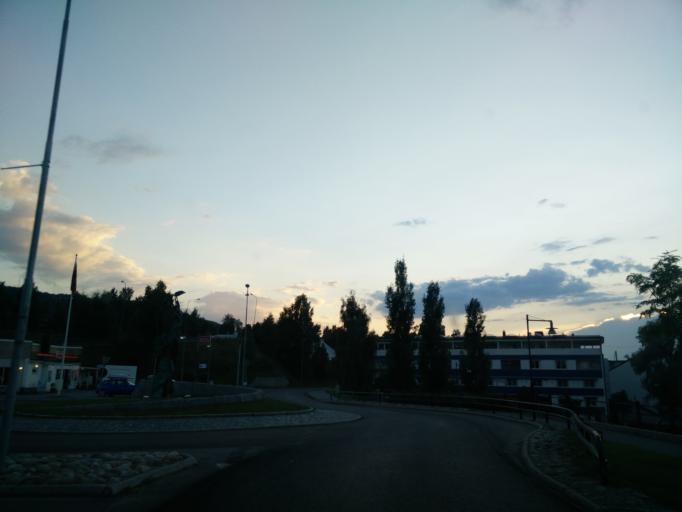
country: SE
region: Vaesternorrland
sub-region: Solleftea Kommun
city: Solleftea
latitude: 63.1658
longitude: 17.2737
